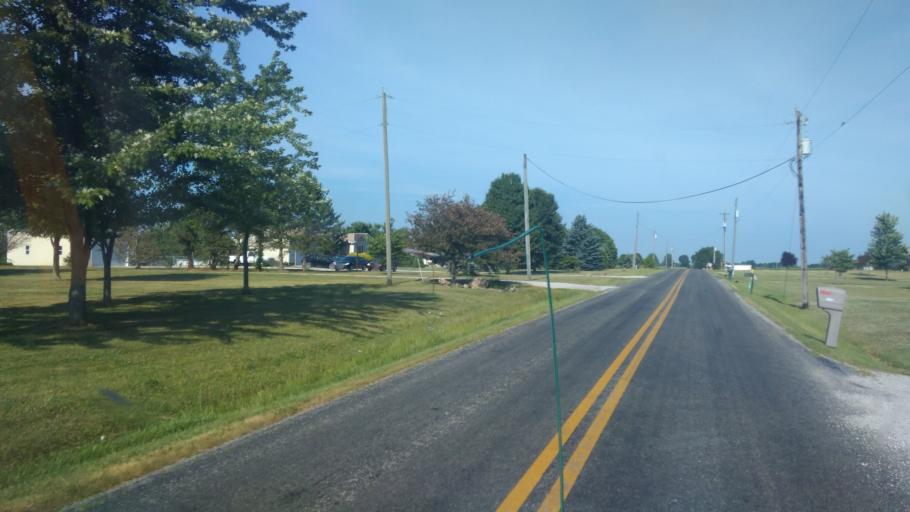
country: US
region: Ohio
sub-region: Delaware County
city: Delaware
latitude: 40.3393
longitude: -83.0060
